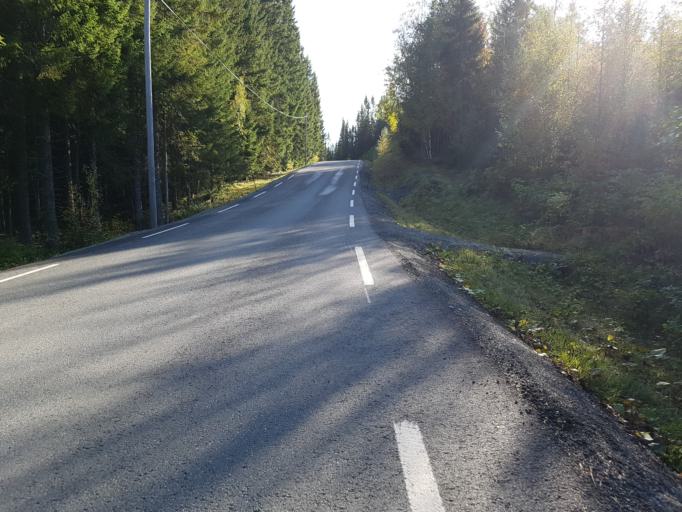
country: NO
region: Sor-Trondelag
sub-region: Malvik
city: Malvik
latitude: 63.3796
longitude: 10.6005
